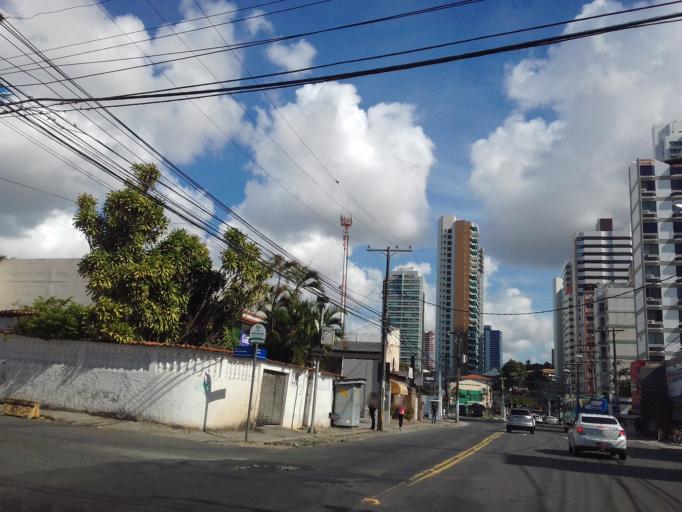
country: BR
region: Bahia
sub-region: Salvador
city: Salvador
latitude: -12.9919
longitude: -38.4546
